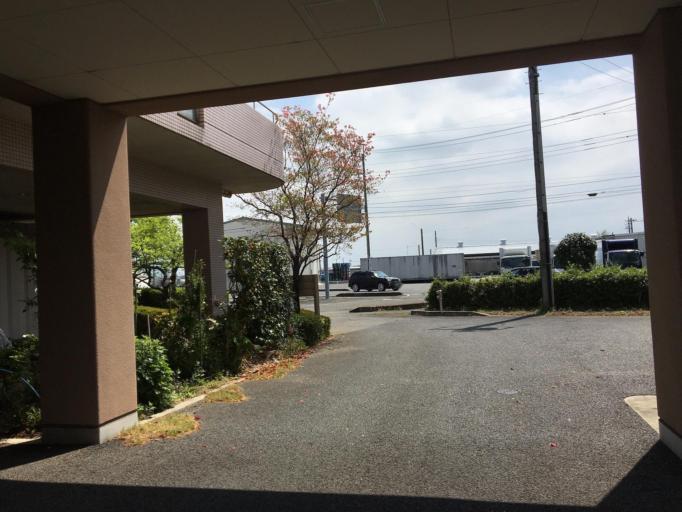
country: JP
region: Gunma
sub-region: Sawa-gun
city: Tamamura
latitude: 36.2889
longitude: 139.1509
